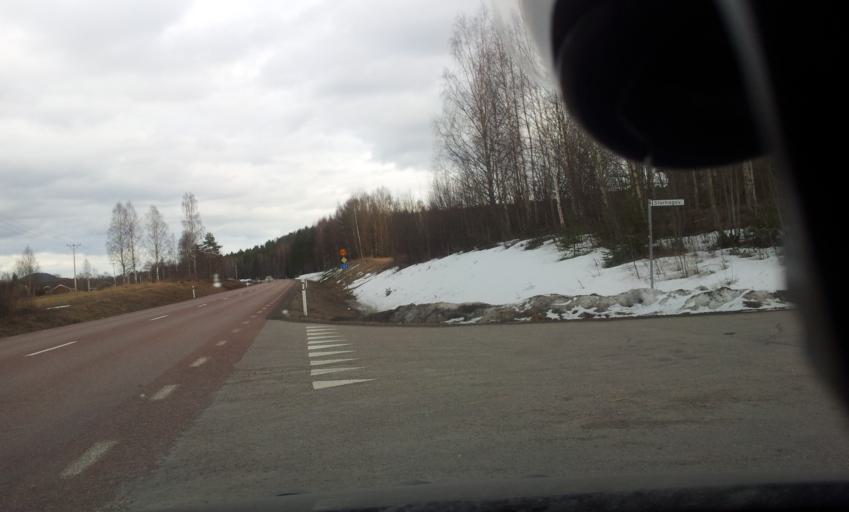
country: SE
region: Gaevleborg
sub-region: Ljusdals Kommun
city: Ljusdal
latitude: 61.8157
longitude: 16.0781
